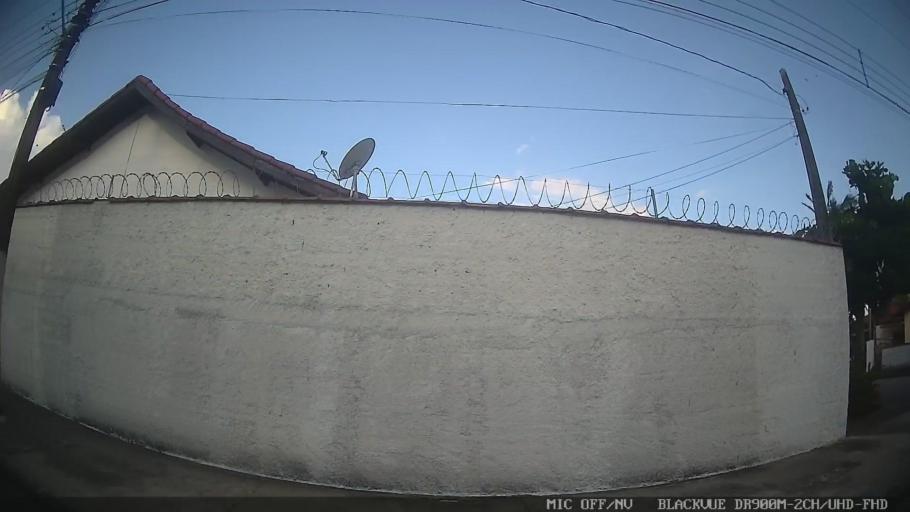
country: BR
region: Sao Paulo
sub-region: Caraguatatuba
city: Caraguatatuba
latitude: -23.6803
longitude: -45.4331
